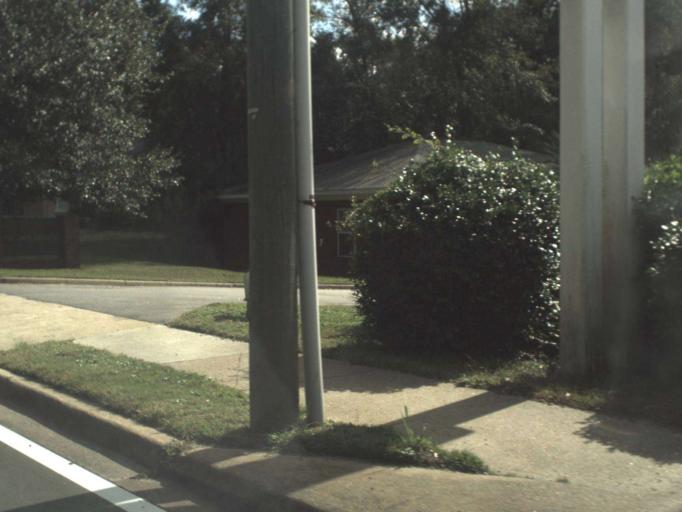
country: US
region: Florida
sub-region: Jackson County
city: Marianna
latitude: 30.7791
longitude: -85.2386
